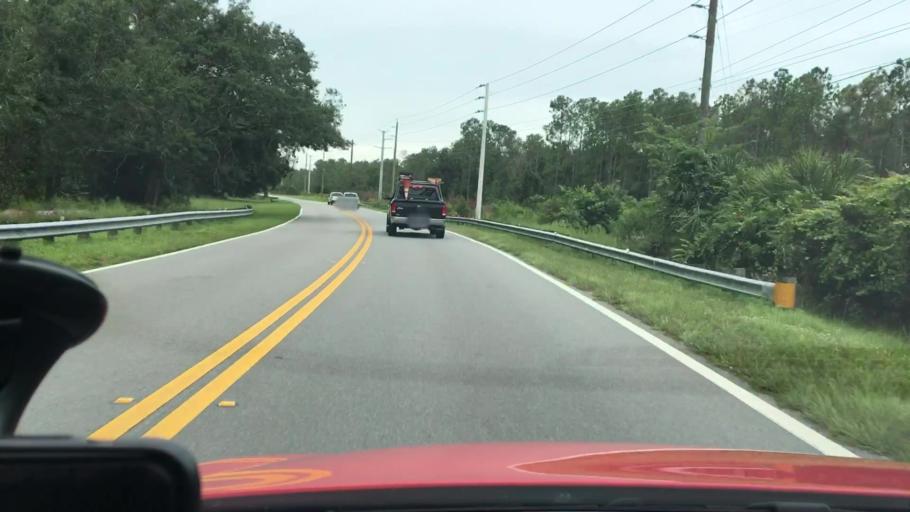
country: US
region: Florida
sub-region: Flagler County
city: Palm Coast
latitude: 29.5288
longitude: -81.2021
